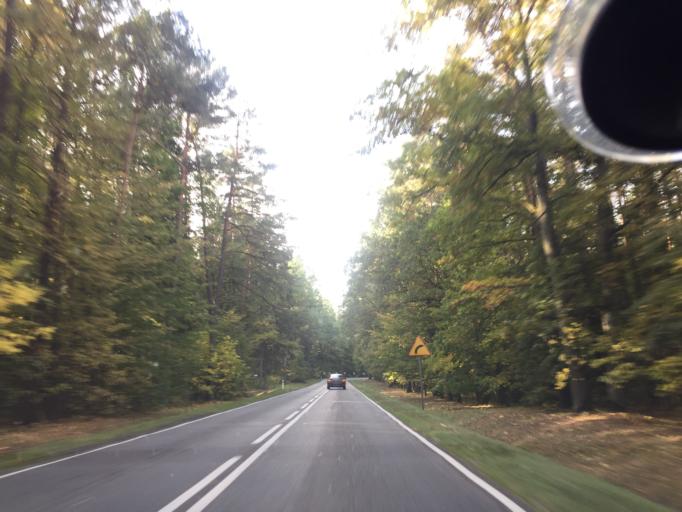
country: PL
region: Warmian-Masurian Voivodeship
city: Dobre Miasto
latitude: 54.0373
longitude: 20.4291
